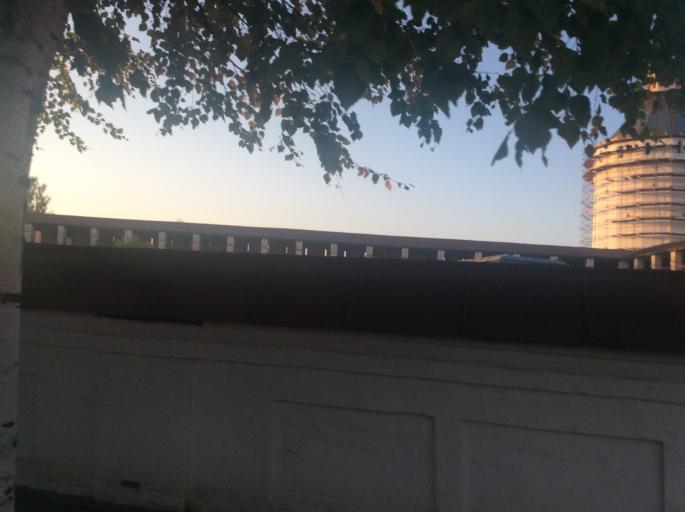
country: RU
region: Vologda
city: Kirillov
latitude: 59.8582
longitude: 38.3701
